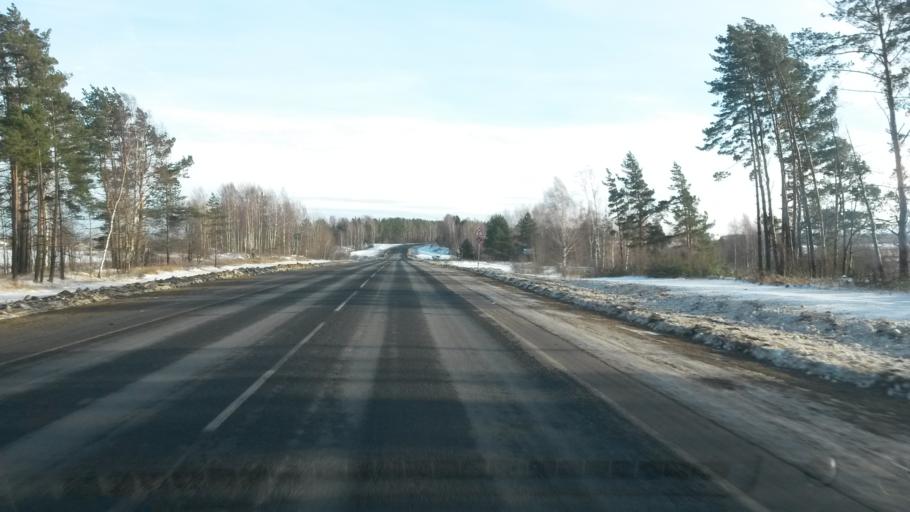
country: RU
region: Jaroslavl
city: Levashevo
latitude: 57.6431
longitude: 40.4996
